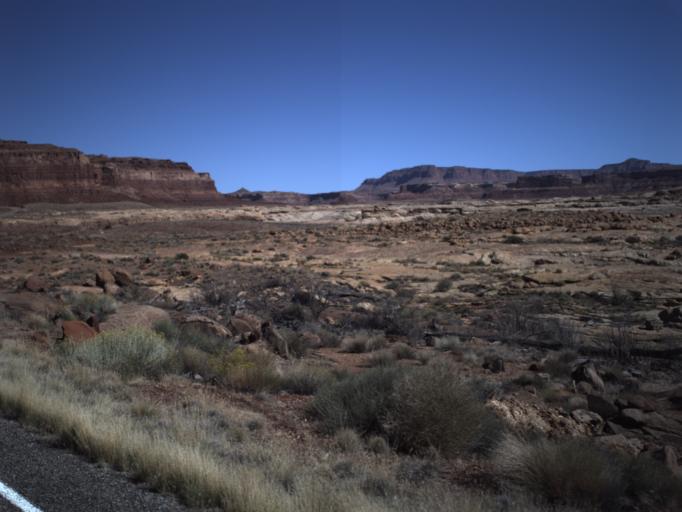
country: US
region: Utah
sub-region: San Juan County
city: Blanding
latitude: 37.9043
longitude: -110.4001
